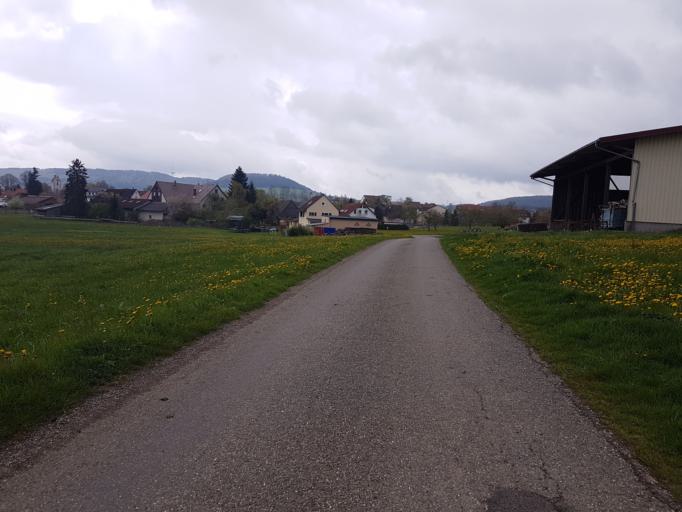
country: DE
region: Baden-Wuerttemberg
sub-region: Freiburg Region
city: Hufingen
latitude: 47.9105
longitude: 8.5337
